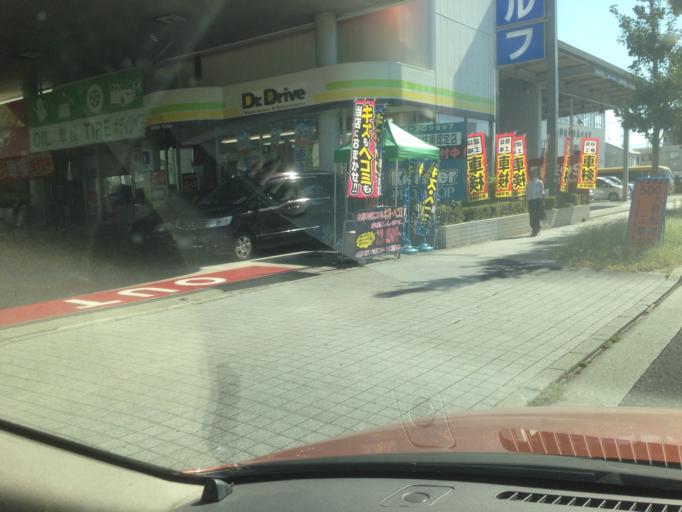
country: JP
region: Tokyo
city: Hachioji
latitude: 35.5816
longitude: 139.3570
